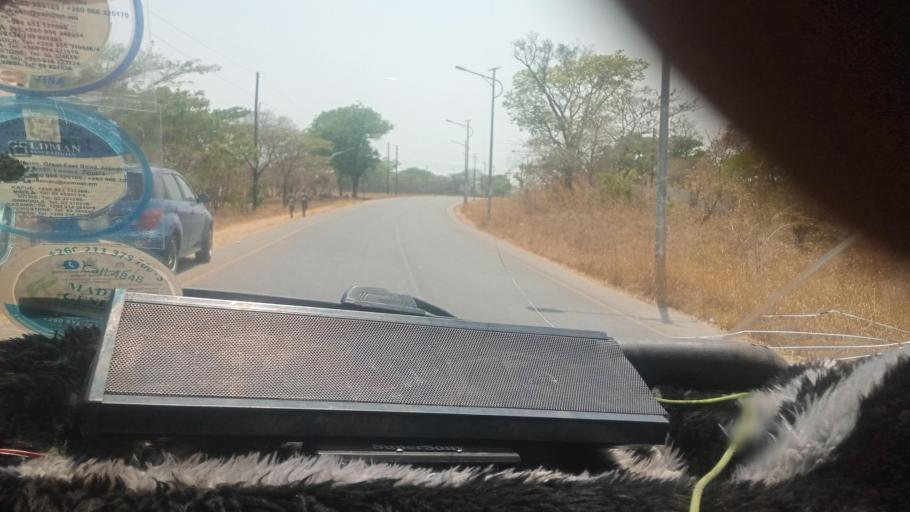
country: ZM
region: Lusaka
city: Lusaka
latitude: -15.4694
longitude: 28.4278
